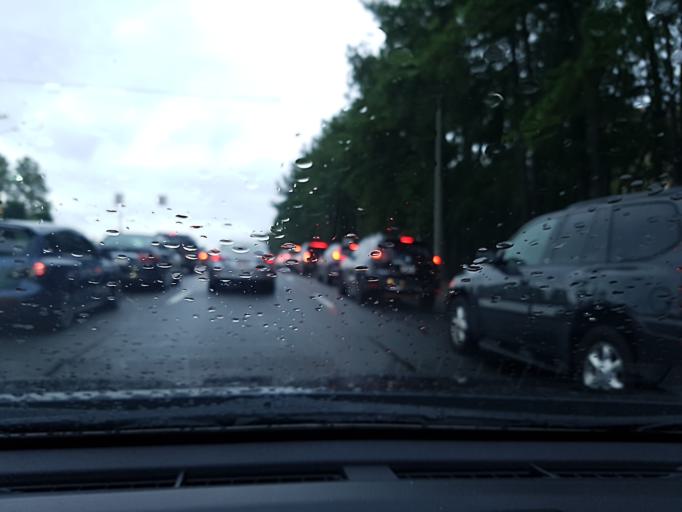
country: US
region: Georgia
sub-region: Gwinnett County
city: Duluth
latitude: 33.9494
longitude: -84.1282
